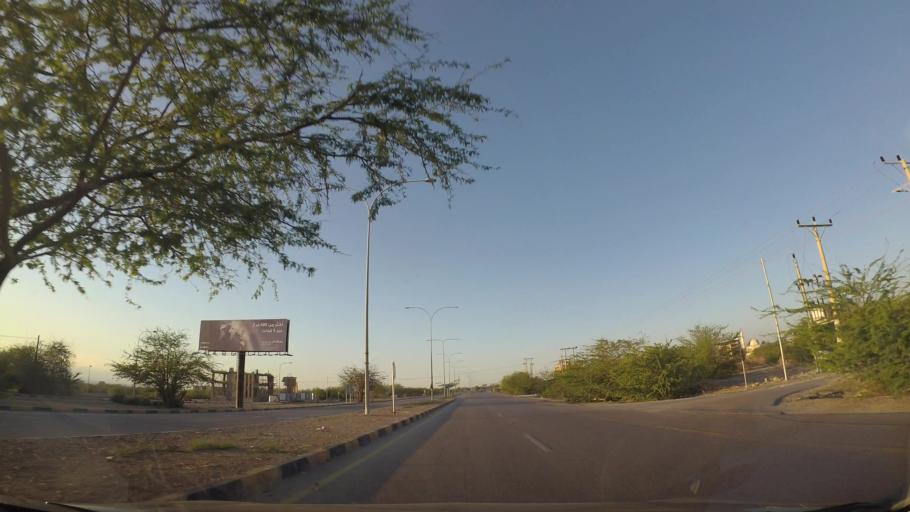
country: PS
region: West Bank
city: Jericho
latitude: 31.7589
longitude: 35.5933
